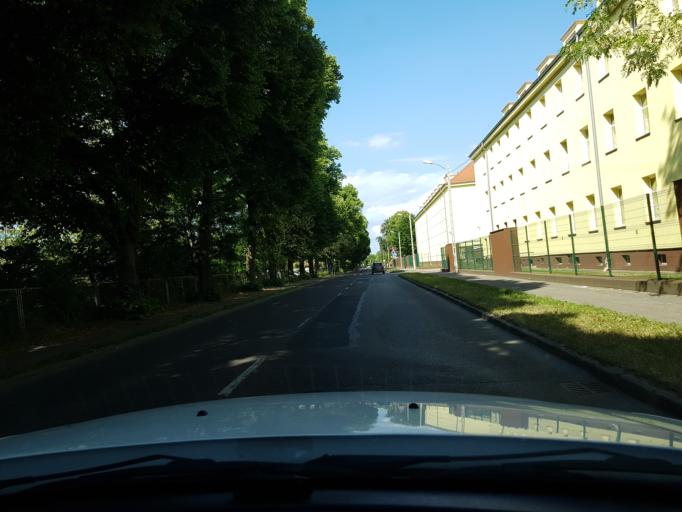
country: PL
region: West Pomeranian Voivodeship
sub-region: Szczecin
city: Szczecin
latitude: 53.3620
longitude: 14.5894
